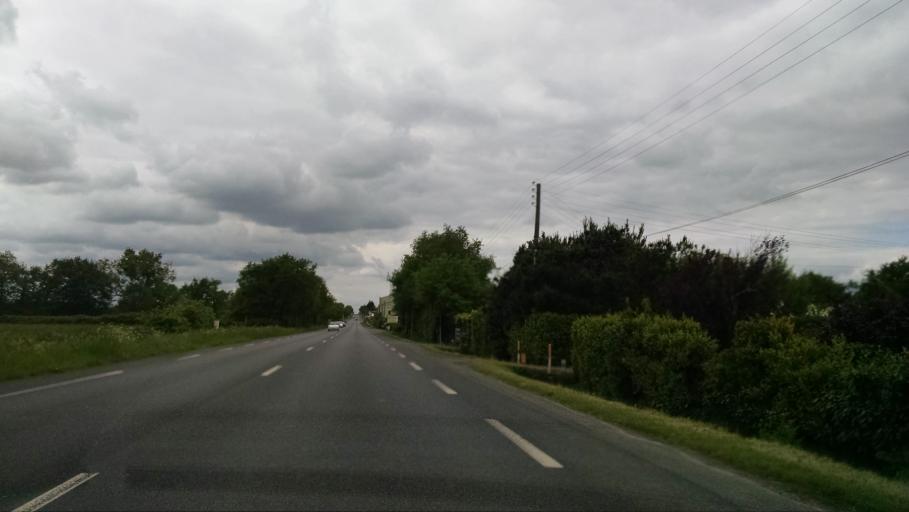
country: FR
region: Pays de la Loire
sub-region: Departement de la Loire-Atlantique
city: Aigrefeuille-sur-Maine
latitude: 47.0905
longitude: -1.4346
